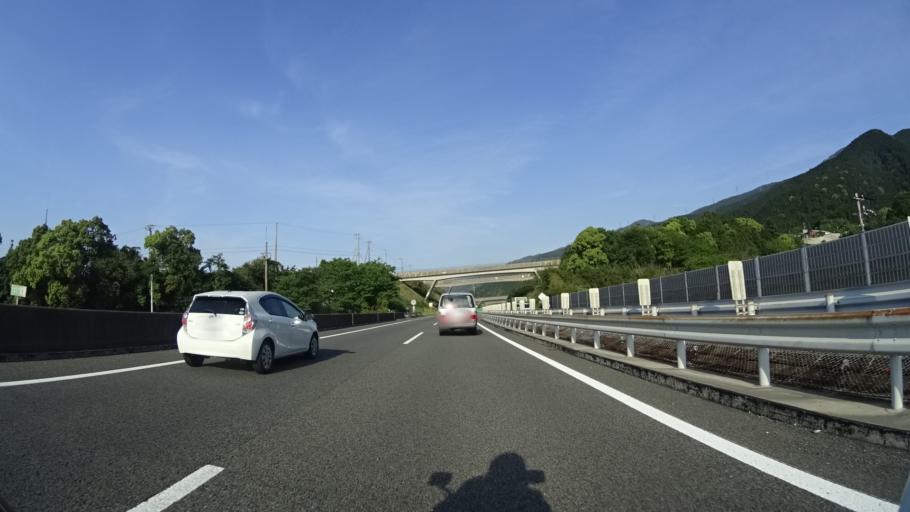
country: JP
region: Ehime
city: Kawanoecho
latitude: 33.9596
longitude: 133.4849
